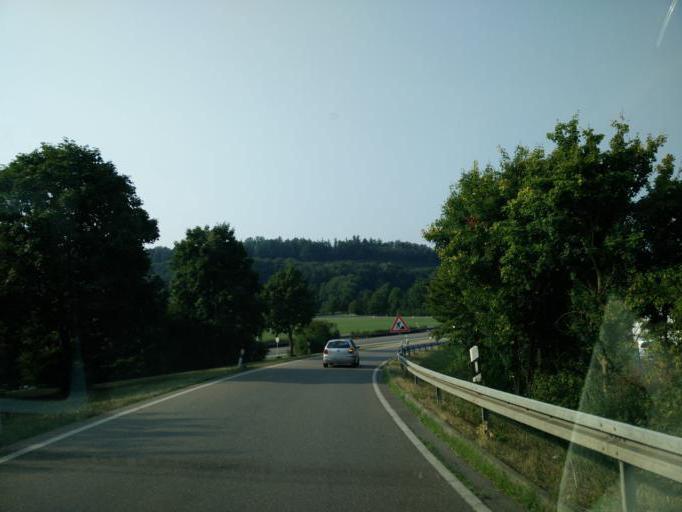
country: DE
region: Baden-Wuerttemberg
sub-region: Tuebingen Region
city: Kusterdingen
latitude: 48.5167
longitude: 9.0874
